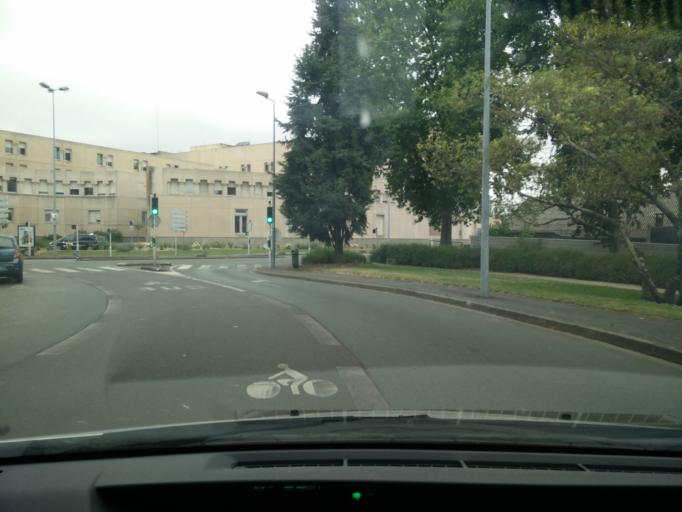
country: FR
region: Pays de la Loire
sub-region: Departement de Maine-et-Loire
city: Angers
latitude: 47.4791
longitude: -0.5553
